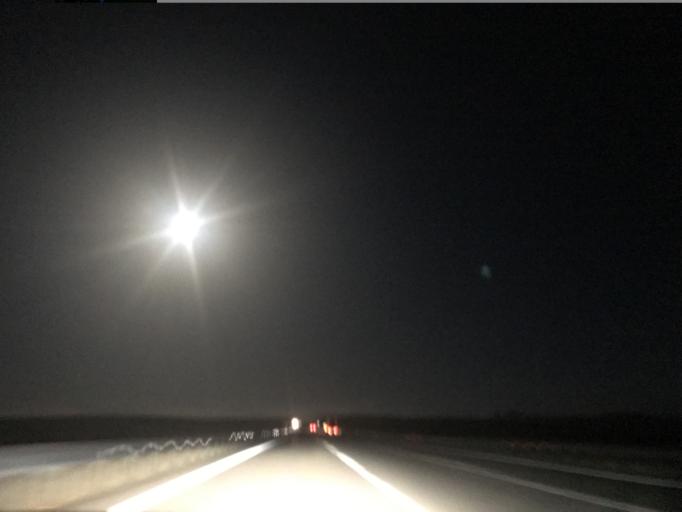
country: TR
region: Nigde
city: Ulukisla
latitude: 37.6384
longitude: 34.3944
